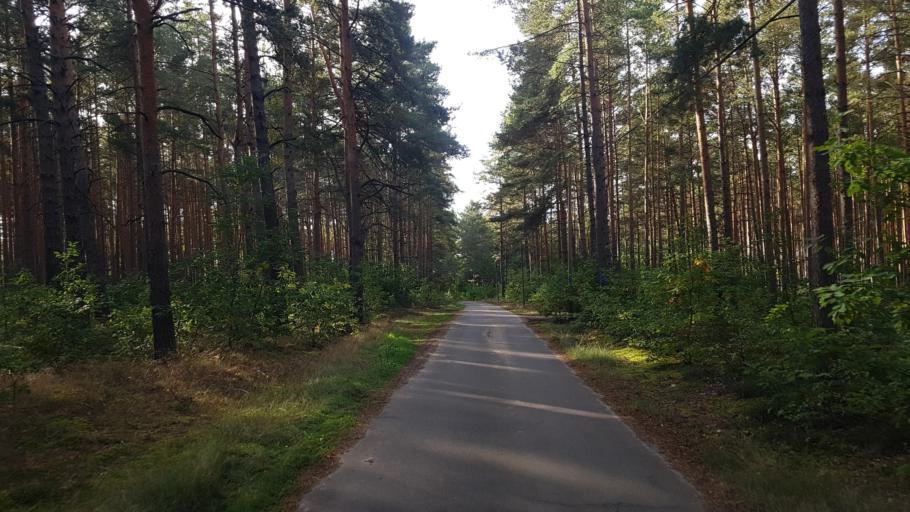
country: DE
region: Brandenburg
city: Hohenbucko
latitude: 51.8230
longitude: 13.5310
